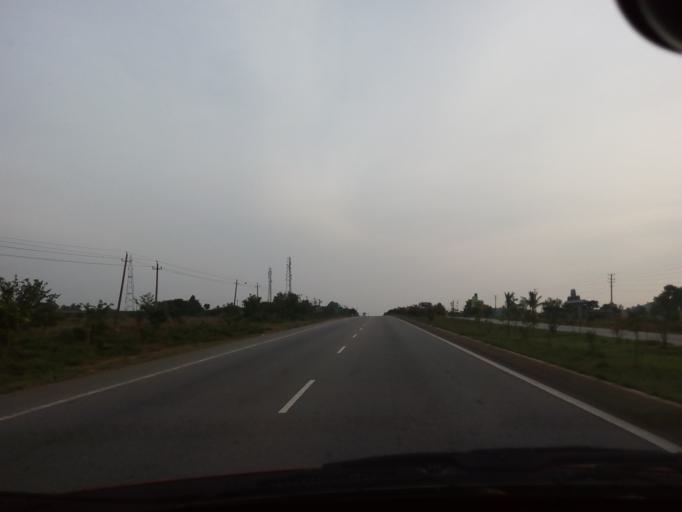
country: IN
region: Karnataka
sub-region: Chikkaballapur
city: Chik Ballapur
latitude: 13.5229
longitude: 77.7650
